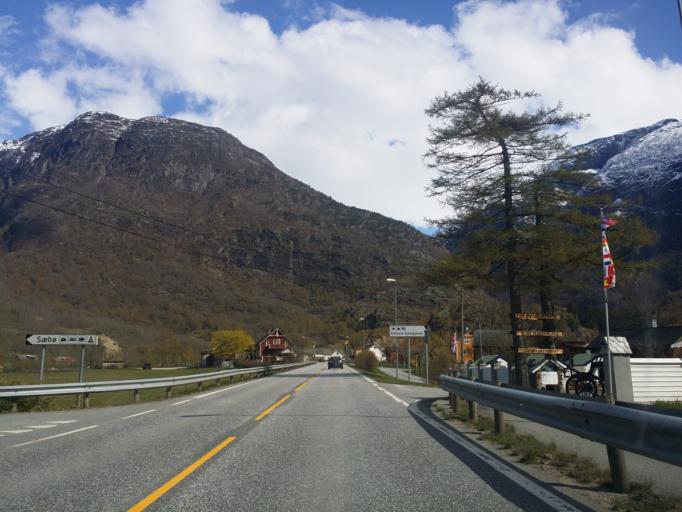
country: NO
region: Hordaland
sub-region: Eidfjord
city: Eidfjord
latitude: 60.4241
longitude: 7.1234
